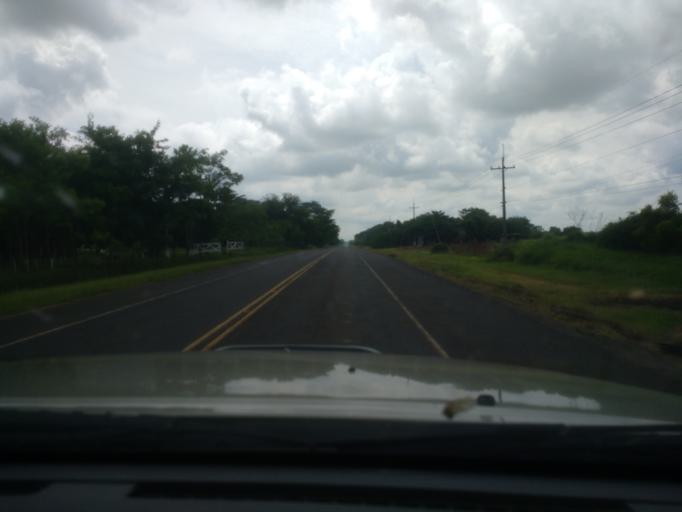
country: PY
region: San Pedro
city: Puerto Rosario
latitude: -24.4255
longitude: -57.0797
